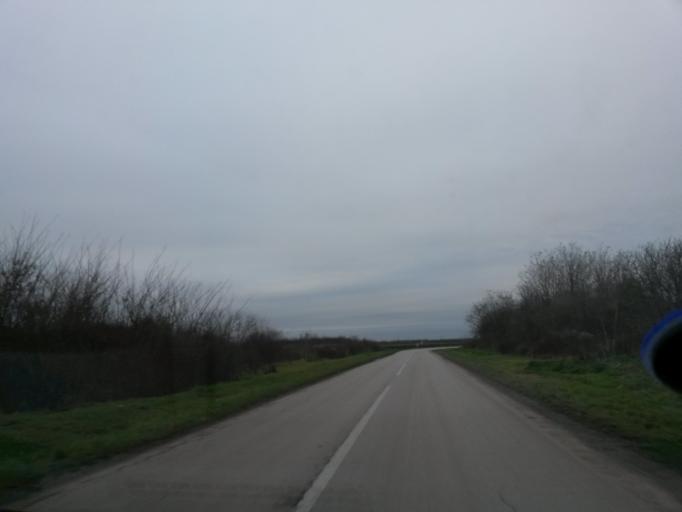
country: HR
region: Osjecko-Baranjska
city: Antunovac
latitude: 45.4783
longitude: 18.7085
